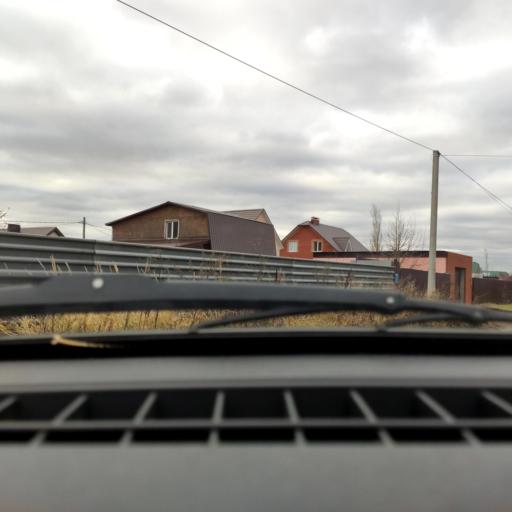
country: RU
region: Bashkortostan
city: Iglino
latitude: 54.7908
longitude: 56.2489
